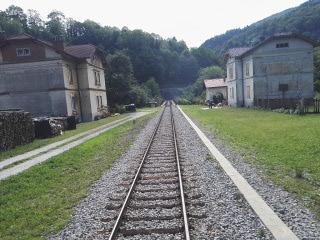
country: SI
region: Tolmin
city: Tolmin
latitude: 46.1592
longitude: 13.8148
